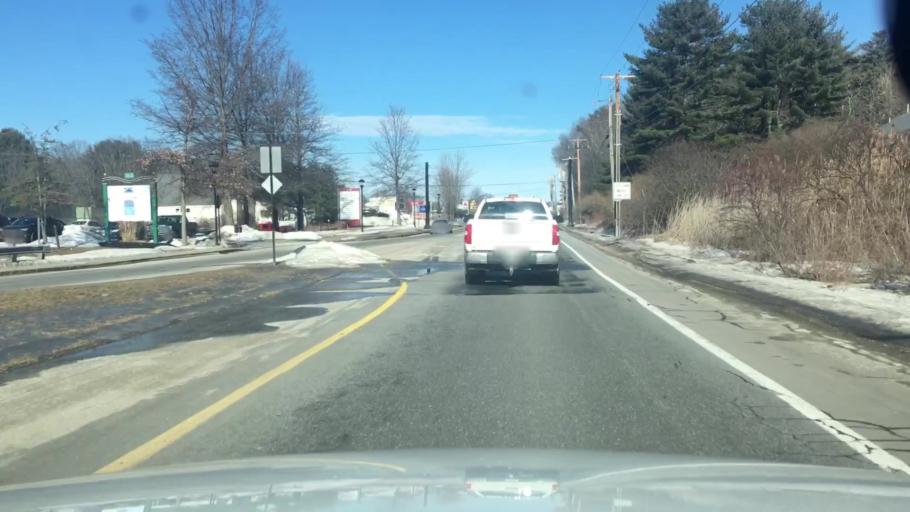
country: US
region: Maine
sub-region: Cumberland County
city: Falmouth
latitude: 43.7121
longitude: -70.2339
